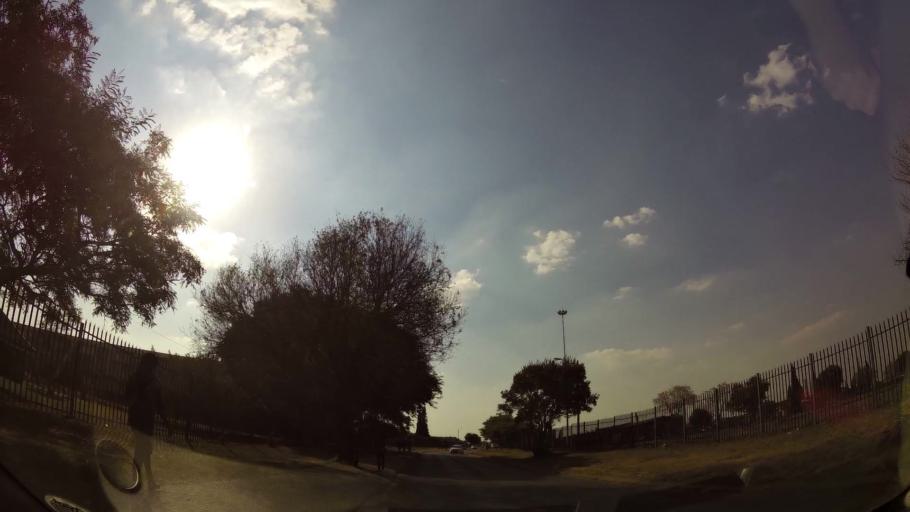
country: ZA
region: Gauteng
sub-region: Ekurhuleni Metropolitan Municipality
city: Benoni
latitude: -26.1561
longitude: 28.4005
